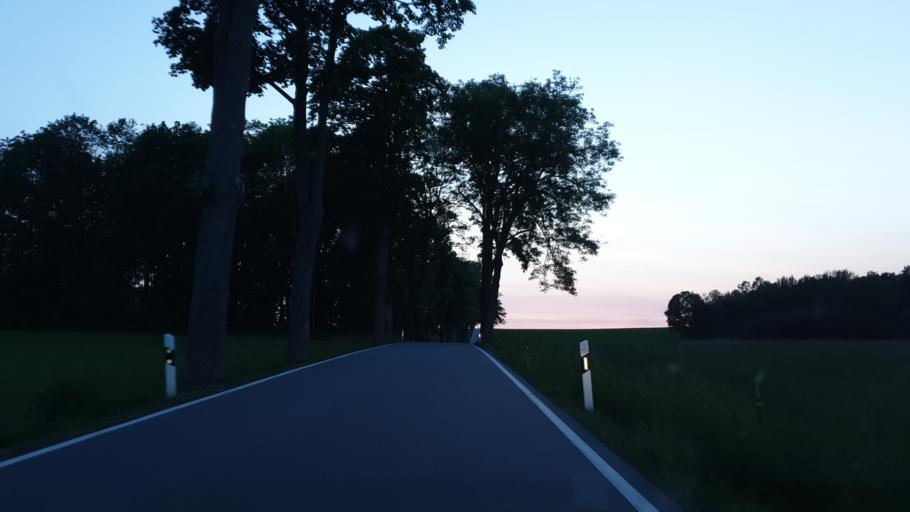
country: DE
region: Saxony
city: Zschorlau
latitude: 50.5540
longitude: 12.6566
